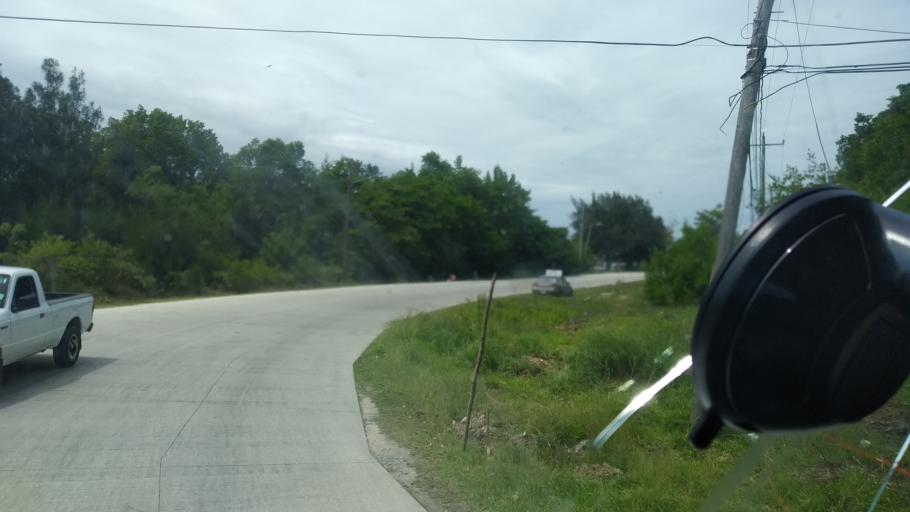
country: BZ
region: Belize
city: Belize City
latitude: 17.5106
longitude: -88.1994
